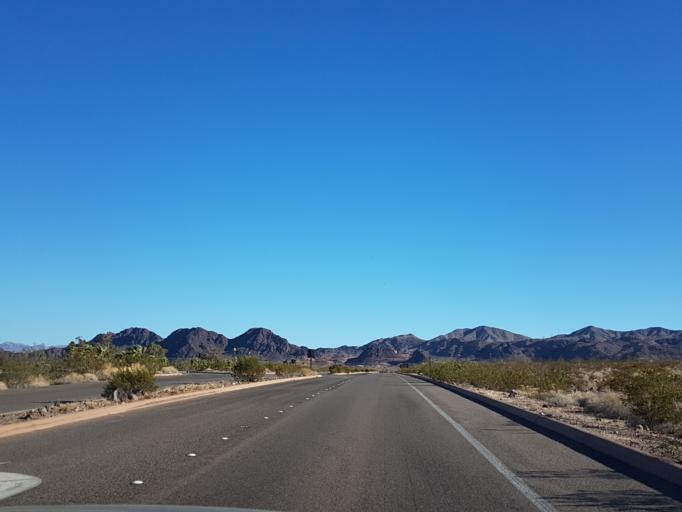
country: US
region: Nevada
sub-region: Clark County
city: Boulder City
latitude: 36.0375
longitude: -114.8056
